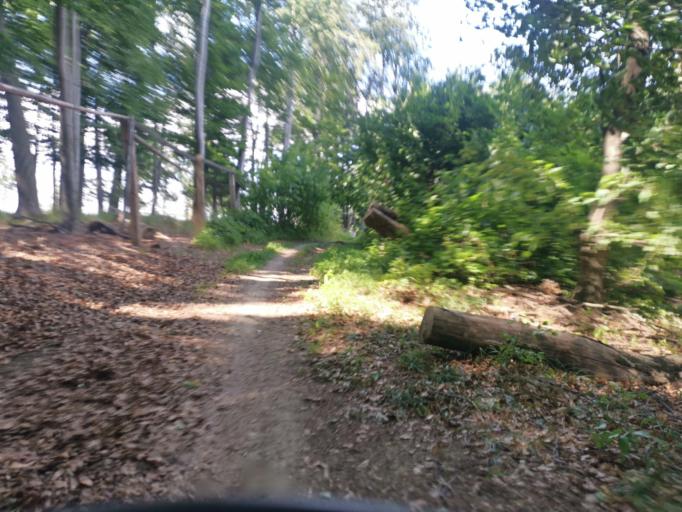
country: CZ
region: South Moravian
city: Knezdub
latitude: 48.8201
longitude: 17.4026
